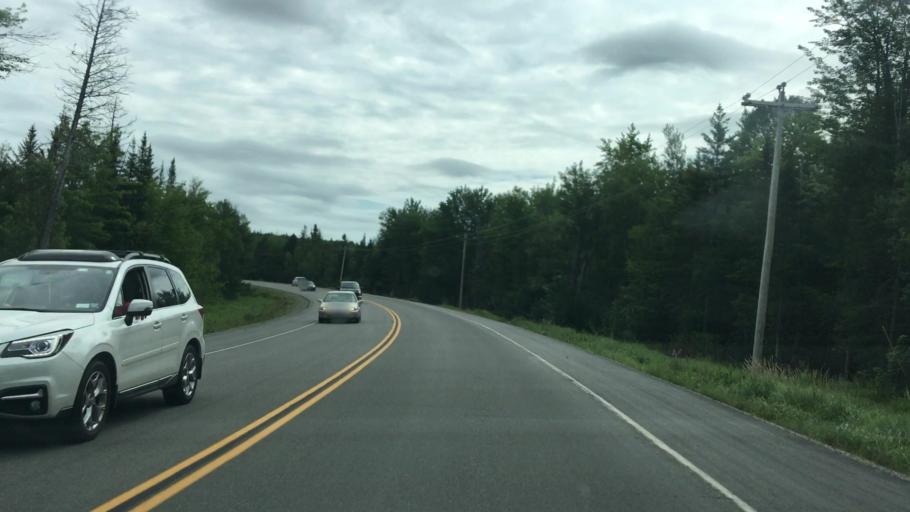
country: US
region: Maine
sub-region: Washington County
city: Machias
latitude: 44.9985
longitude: -67.5671
